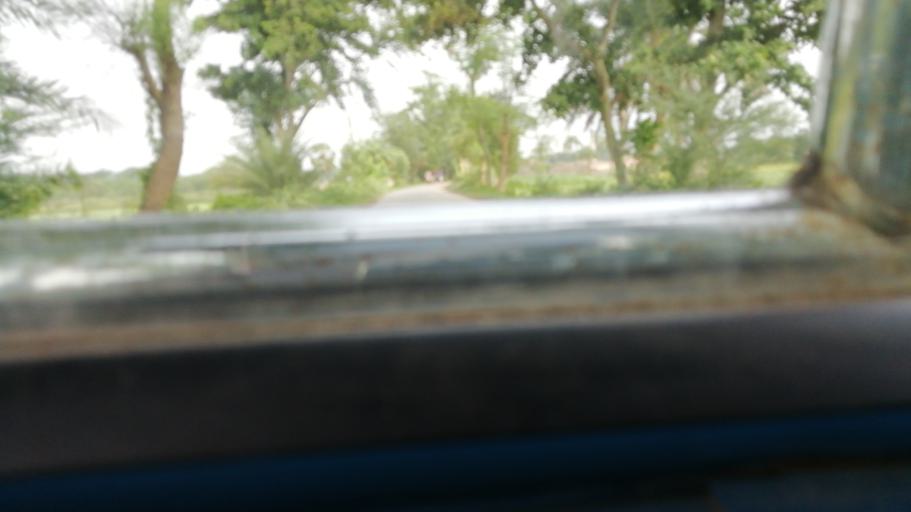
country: BD
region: Khulna
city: Kesabpur
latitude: 23.0261
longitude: 89.2528
